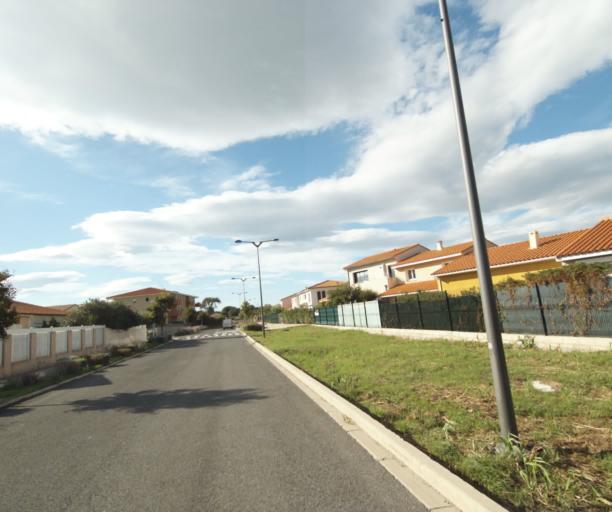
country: FR
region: Languedoc-Roussillon
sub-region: Departement des Pyrenees-Orientales
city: Argelers
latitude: 42.5436
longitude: 3.0387
